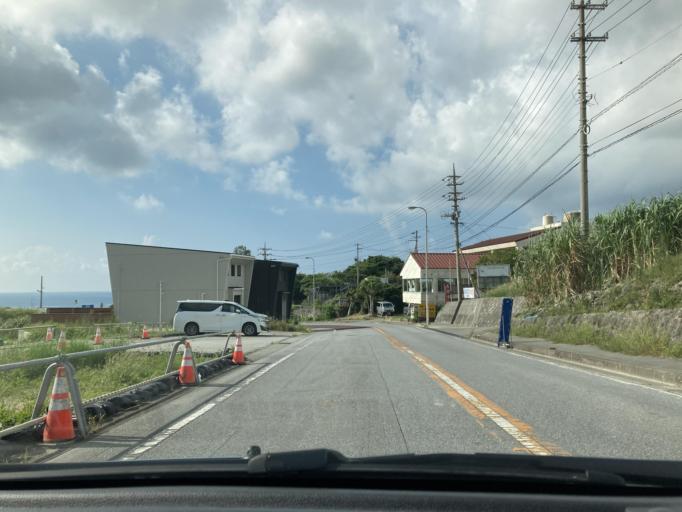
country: JP
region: Okinawa
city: Tomigusuku
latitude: 26.1403
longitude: 127.7665
